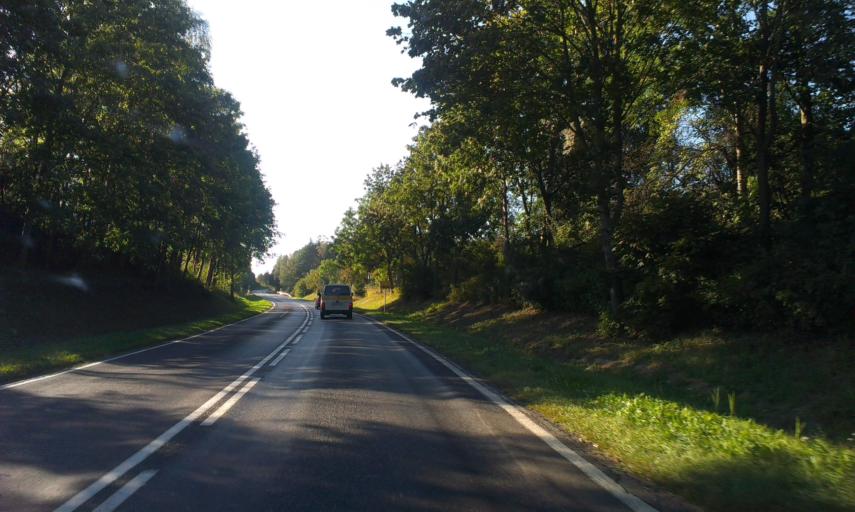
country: PL
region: Kujawsko-Pomorskie
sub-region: Powiat swiecki
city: Swiecie
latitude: 53.4129
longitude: 18.3704
